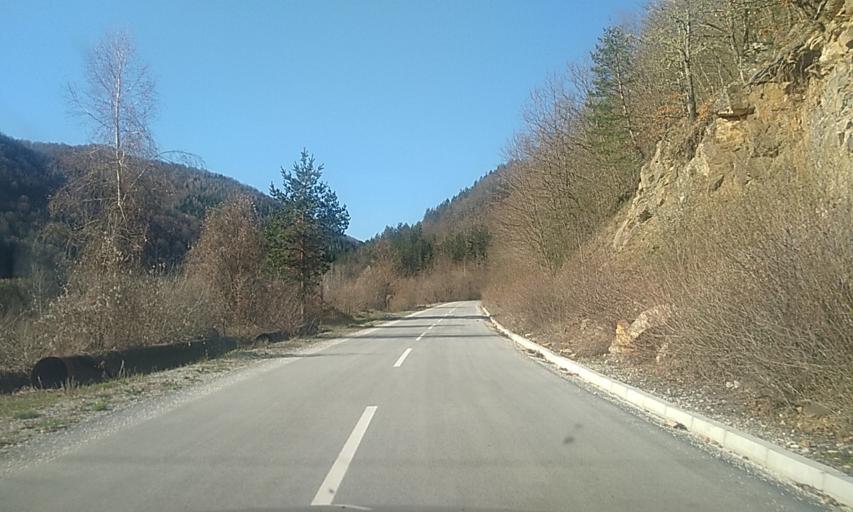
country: RS
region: Central Serbia
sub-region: Pcinjski Okrug
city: Bosilegrad
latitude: 42.3983
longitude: 22.4563
